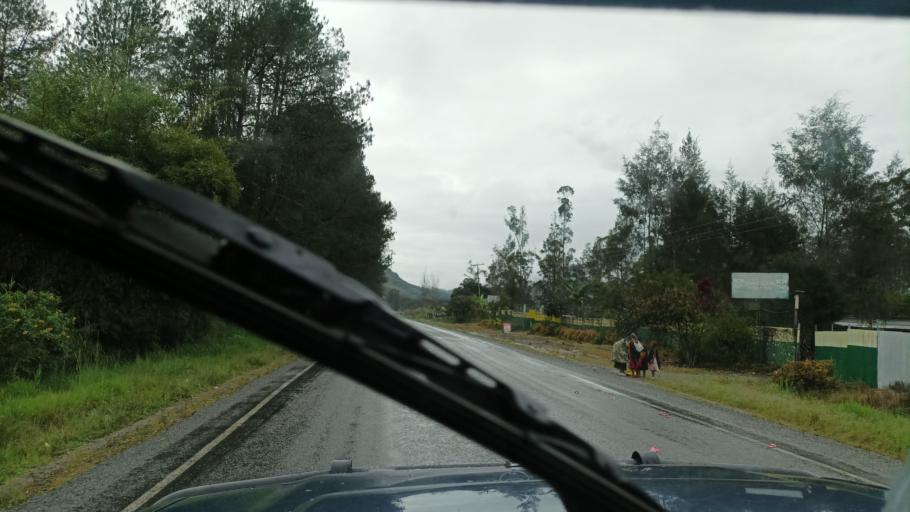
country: PG
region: Western Highlands
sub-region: Hagen
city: Mount Hagen
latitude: -5.8361
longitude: 144.3351
